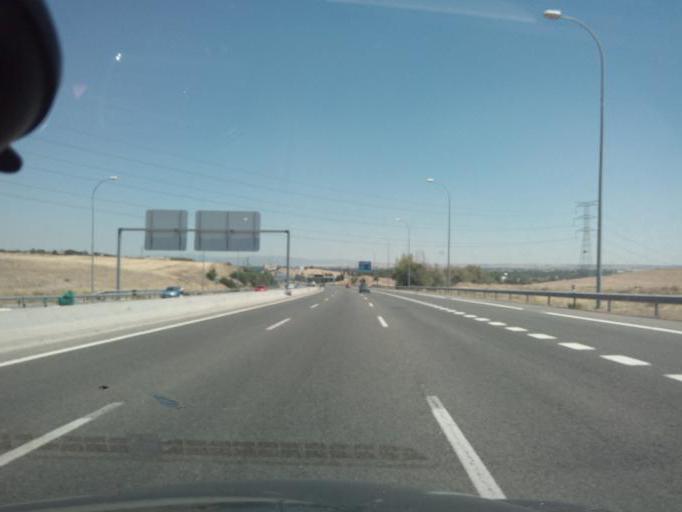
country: ES
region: Madrid
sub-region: Provincia de Madrid
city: San Sebastian de los Reyes
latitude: 40.5675
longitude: -3.5893
